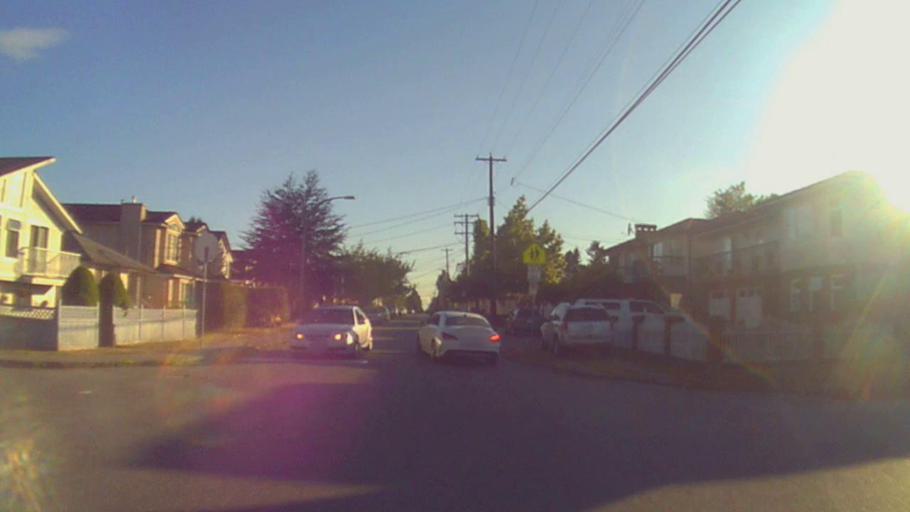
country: CA
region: British Columbia
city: New Westminster
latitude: 49.2263
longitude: -122.9188
